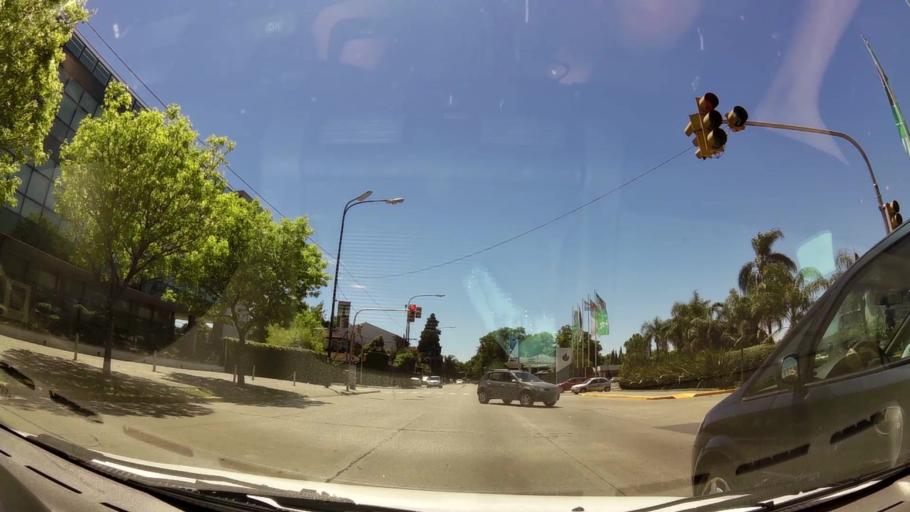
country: AR
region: Buenos Aires
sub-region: Partido de San Isidro
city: San Isidro
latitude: -34.5057
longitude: -58.5269
